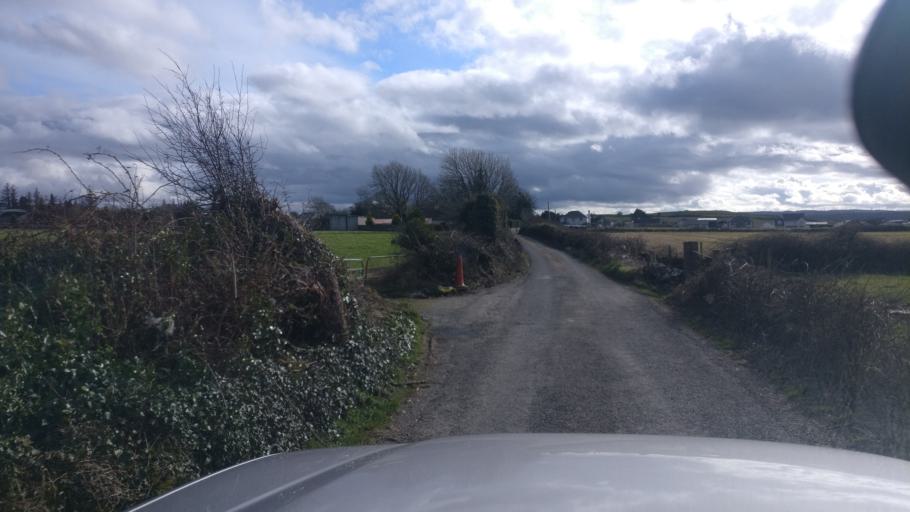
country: IE
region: Connaught
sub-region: County Galway
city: Loughrea
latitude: 53.1954
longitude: -8.5404
